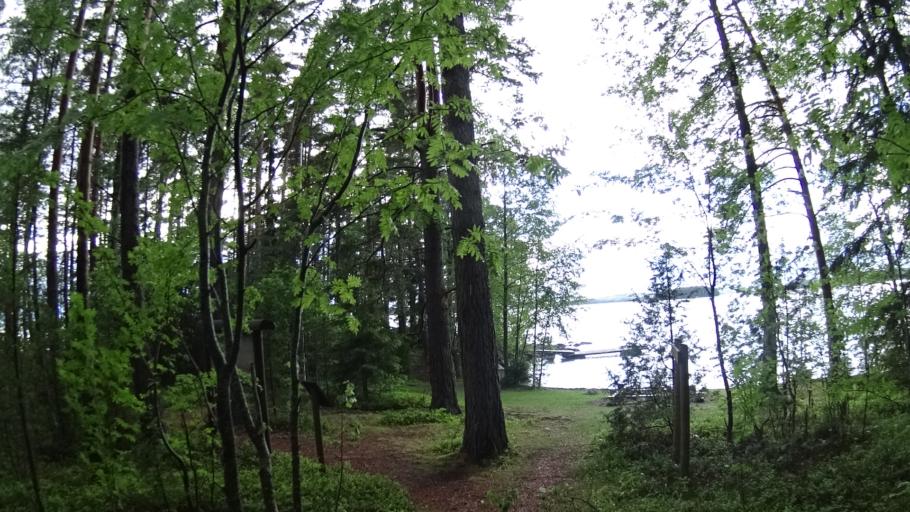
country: FI
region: Paijanne Tavastia
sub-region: Lahti
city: Sysmae
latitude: 61.4823
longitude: 25.5617
